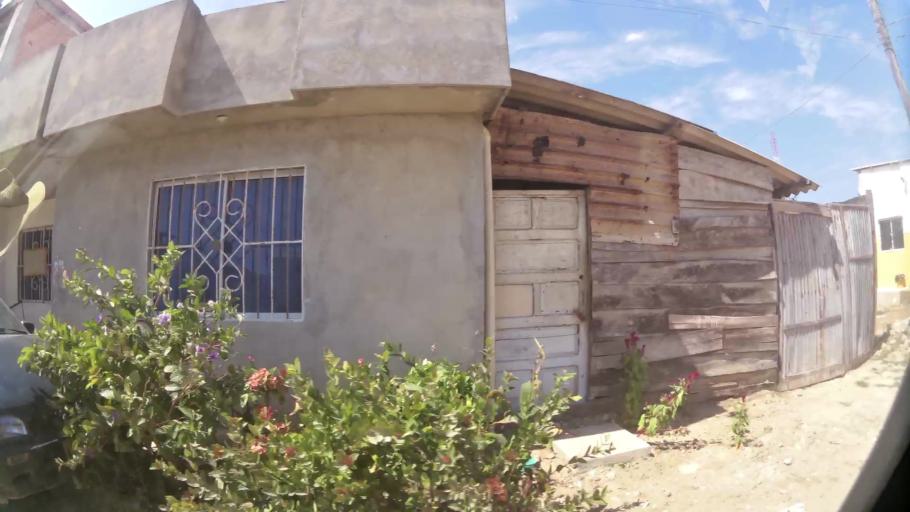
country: CO
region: Atlantico
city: Barranquilla
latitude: 10.9765
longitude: -74.8478
